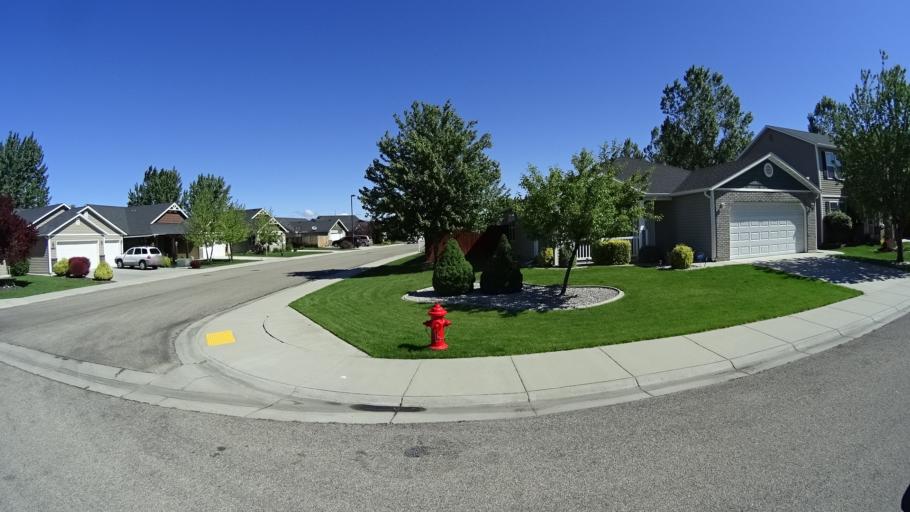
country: US
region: Idaho
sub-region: Ada County
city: Meridian
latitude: 43.6449
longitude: -116.3916
